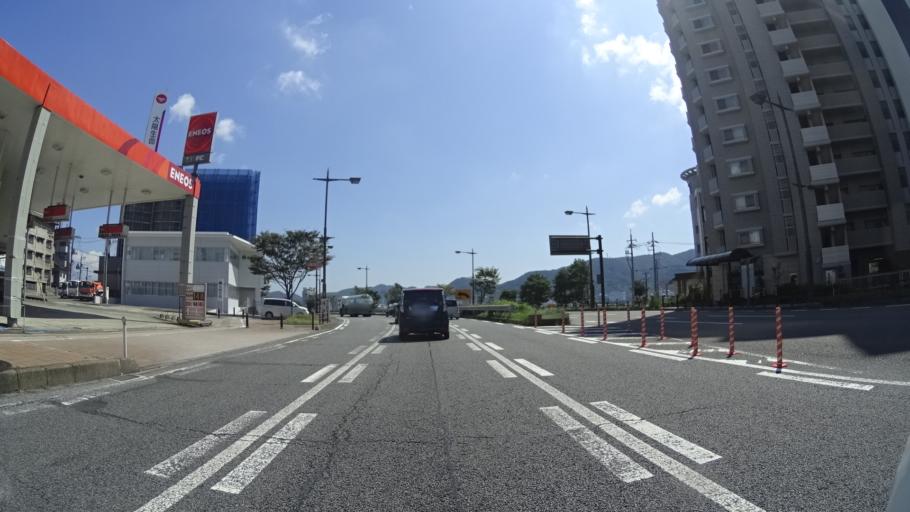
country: JP
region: Yamaguchi
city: Shimonoseki
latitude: 33.9519
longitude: 130.9369
